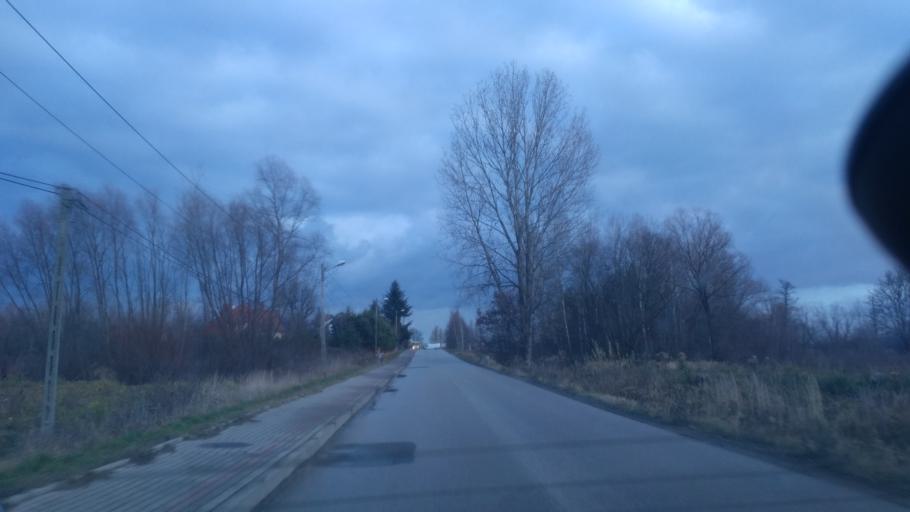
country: PL
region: Subcarpathian Voivodeship
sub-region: Powiat lancucki
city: Czarna
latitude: 50.1113
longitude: 22.1910
